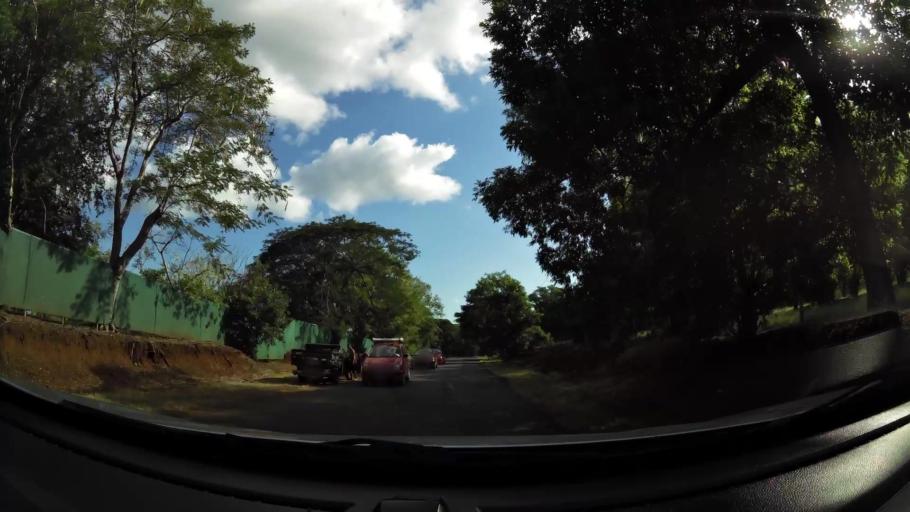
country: CR
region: Guanacaste
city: Sardinal
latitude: 10.5556
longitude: -85.6814
